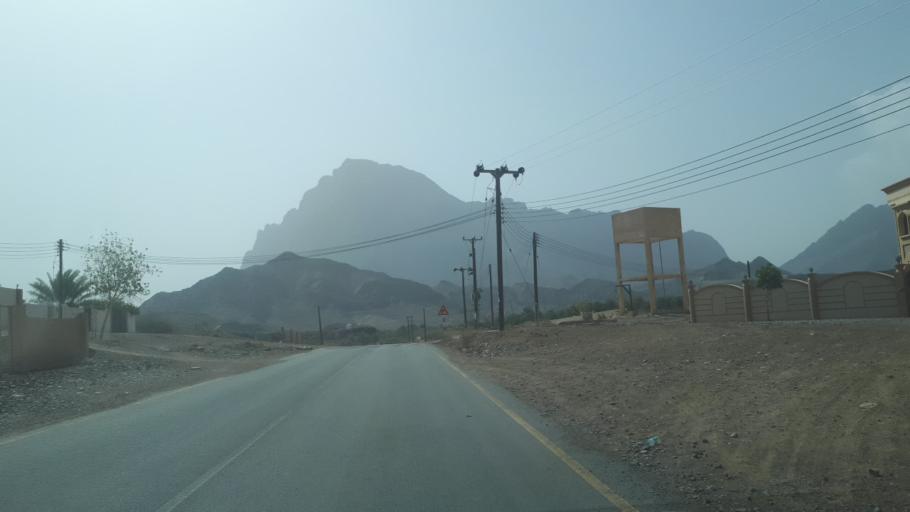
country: OM
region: Muhafazat ad Dakhiliyah
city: Bahla'
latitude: 23.2277
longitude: 57.0471
